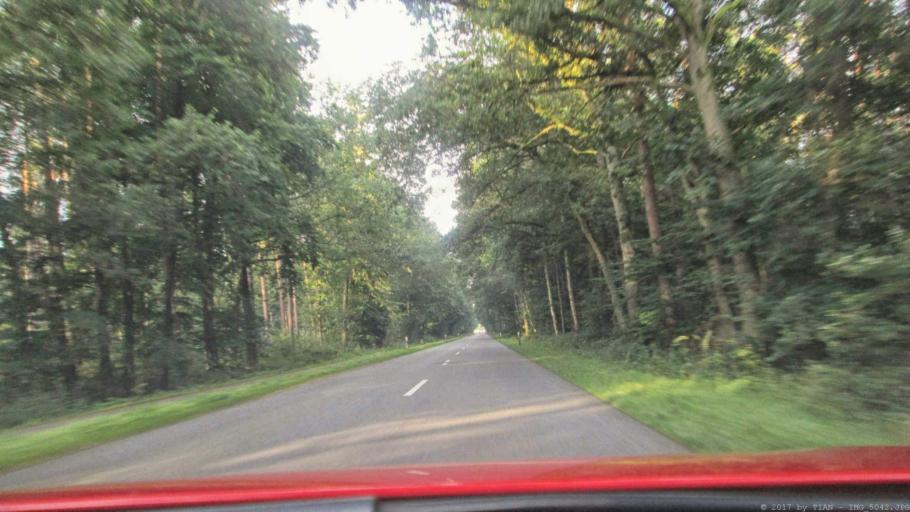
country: DE
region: Lower Saxony
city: Emmendorf
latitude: 53.0003
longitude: 10.5895
